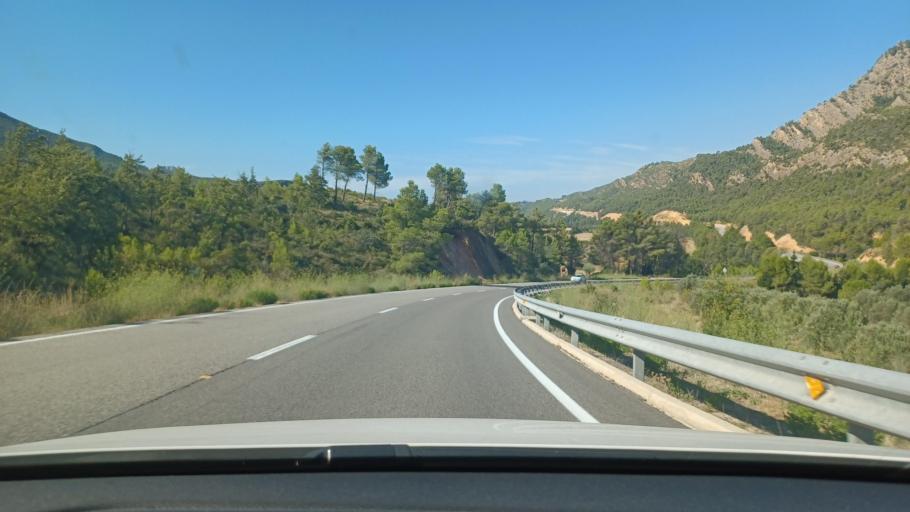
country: ES
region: Catalonia
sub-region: Provincia de Tarragona
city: Horta de Sant Joan
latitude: 40.9602
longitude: 0.3611
